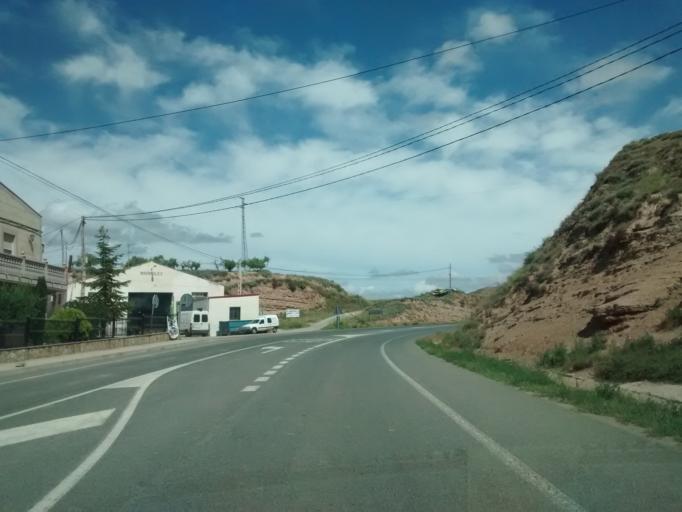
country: ES
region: La Rioja
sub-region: Provincia de La Rioja
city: Leza de Rio Leza
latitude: 42.3609
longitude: -2.3884
